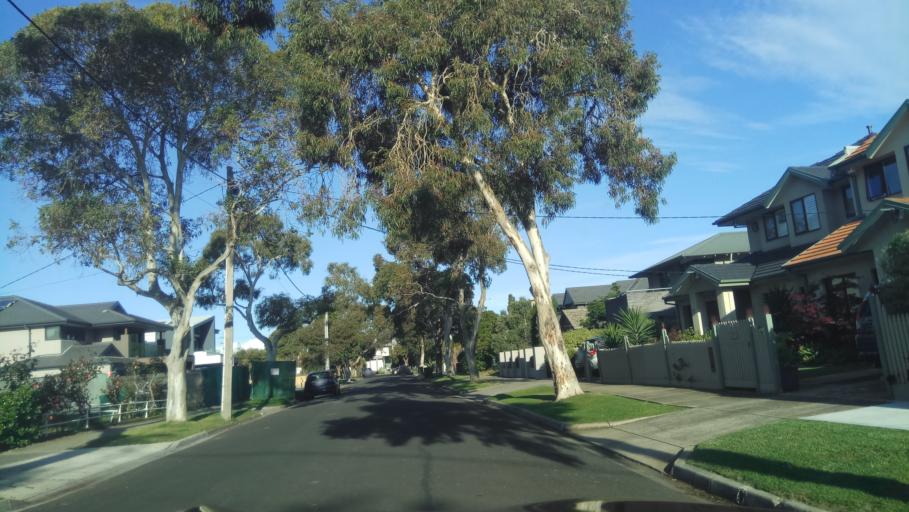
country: AU
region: Victoria
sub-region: Hobsons Bay
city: Williamstown North
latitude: -37.8611
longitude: 144.8846
